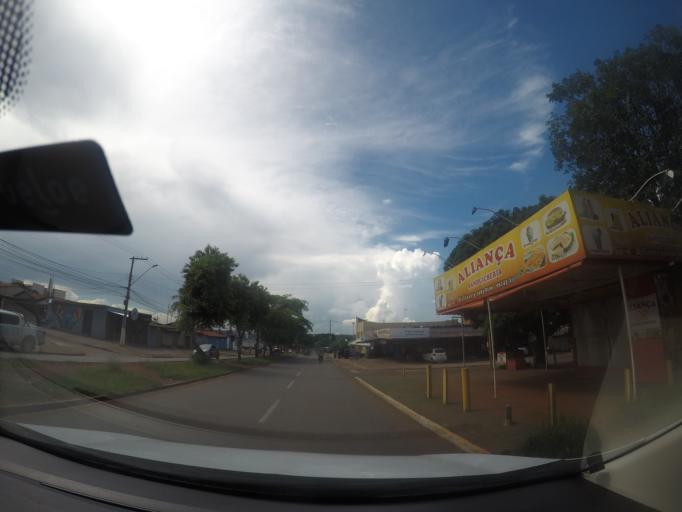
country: BR
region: Goias
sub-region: Trindade
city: Trindade
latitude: -16.6818
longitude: -49.3858
